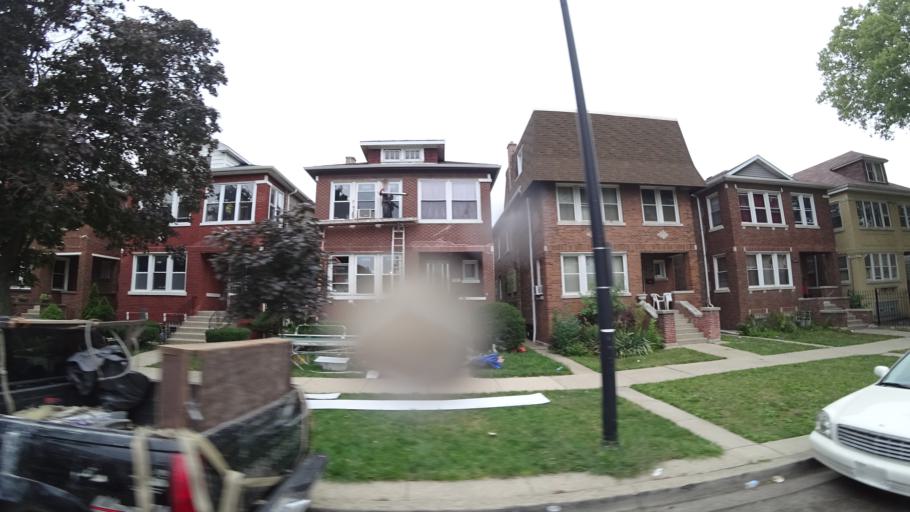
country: US
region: Illinois
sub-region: Cook County
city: Cicero
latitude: 41.8580
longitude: -87.7531
